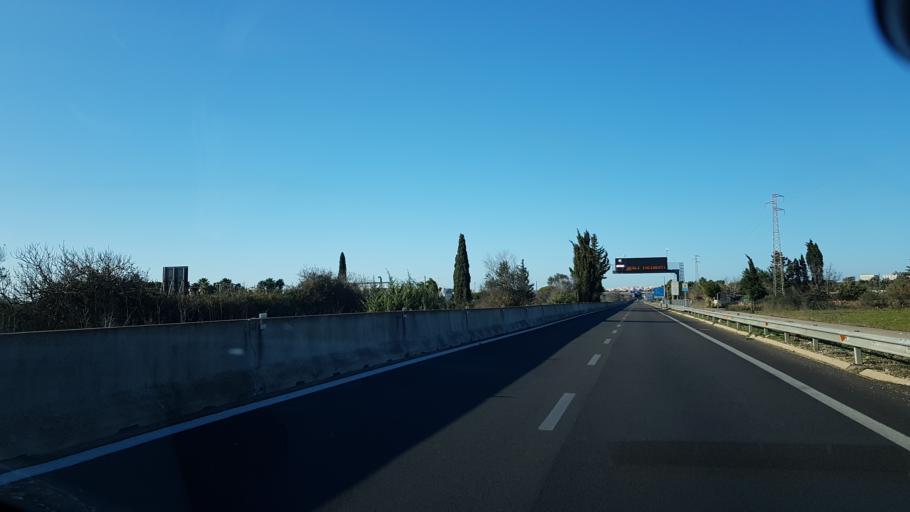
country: IT
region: Apulia
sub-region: Provincia di Lecce
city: Gallipoli
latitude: 40.0347
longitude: 18.0268
